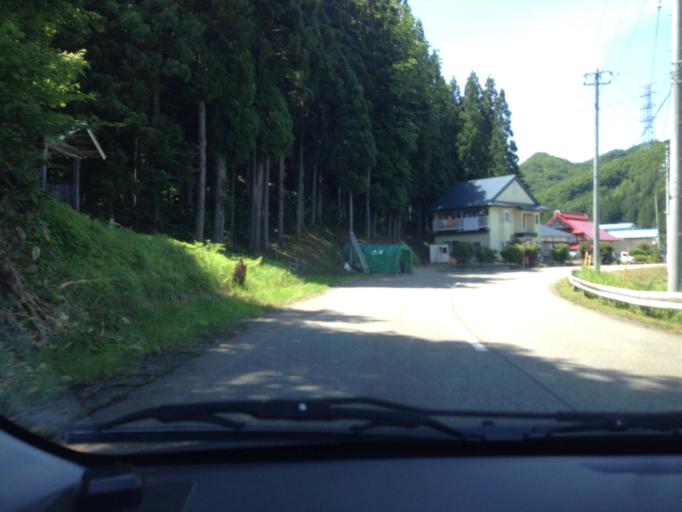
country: JP
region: Tochigi
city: Kuroiso
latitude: 37.2187
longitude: 139.7500
